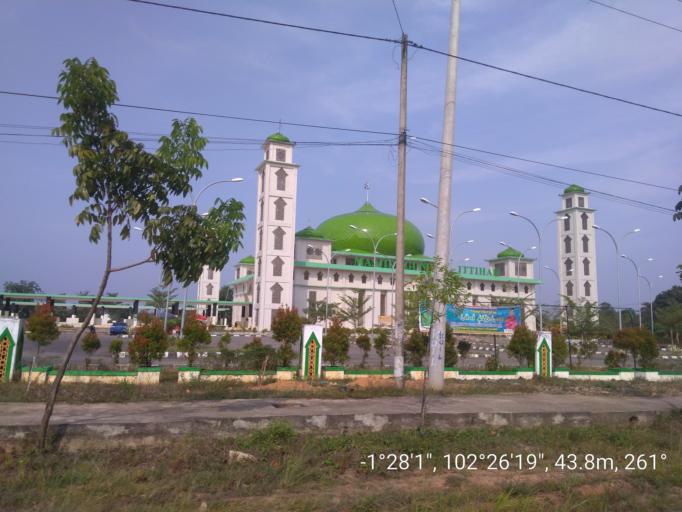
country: ID
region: Jambi
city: Muara Tebo
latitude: -1.4669
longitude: 102.4386
